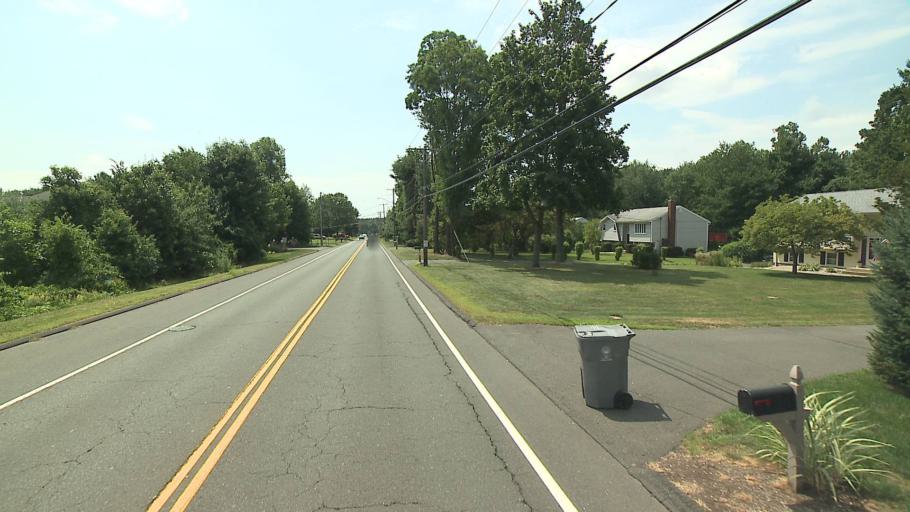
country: US
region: Connecticut
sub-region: Hartford County
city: Plainville
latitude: 41.6966
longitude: -72.8778
